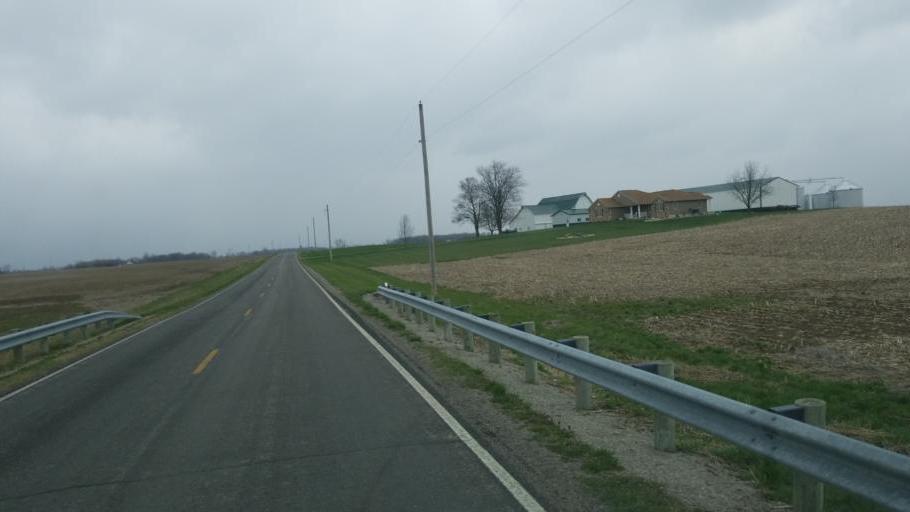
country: US
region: Ohio
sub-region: Union County
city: Richwood
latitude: 40.4395
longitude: -83.3947
